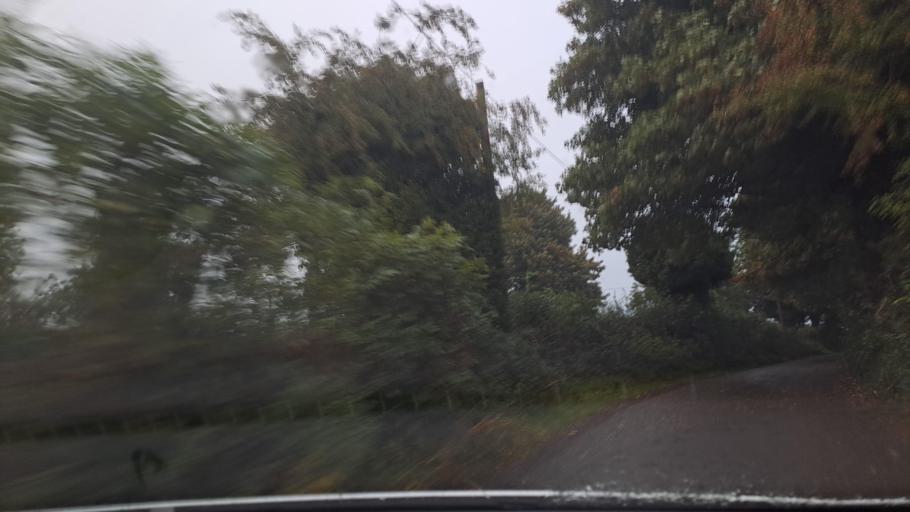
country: IE
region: Ulster
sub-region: County Monaghan
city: Carrickmacross
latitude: 53.9855
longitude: -6.6898
